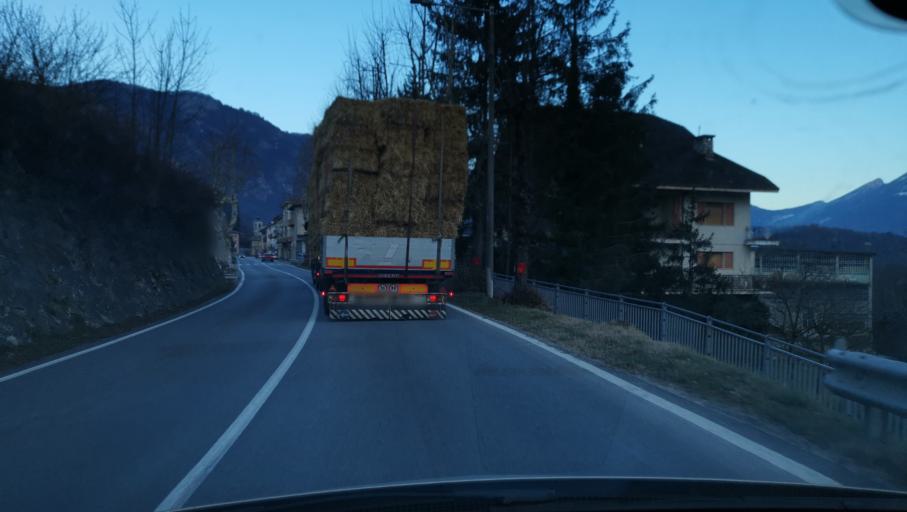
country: IT
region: Piedmont
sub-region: Provincia di Cuneo
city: Demonte
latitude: 44.3132
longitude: 7.2910
